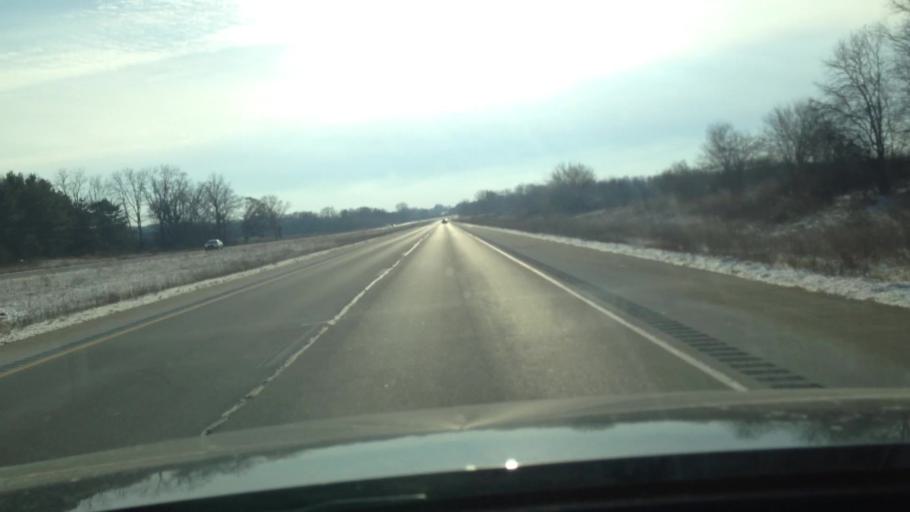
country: US
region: Wisconsin
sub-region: Walworth County
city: Potter Lake
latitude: 42.8171
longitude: -88.3625
